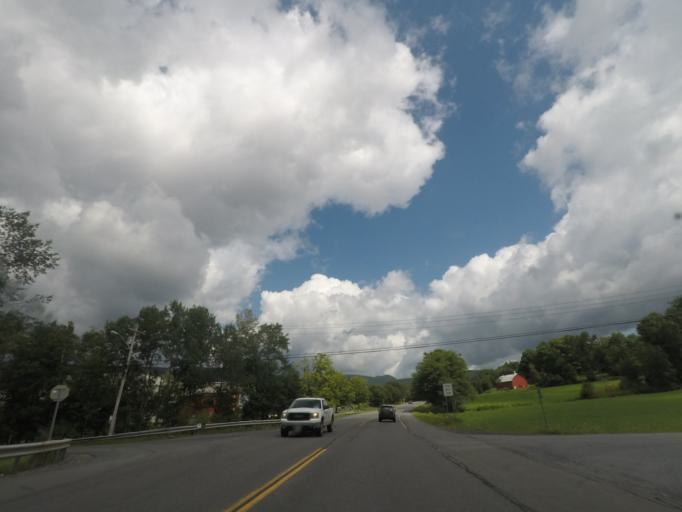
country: US
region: Massachusetts
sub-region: Berkshire County
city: Lanesborough
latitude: 42.6105
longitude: -73.3760
